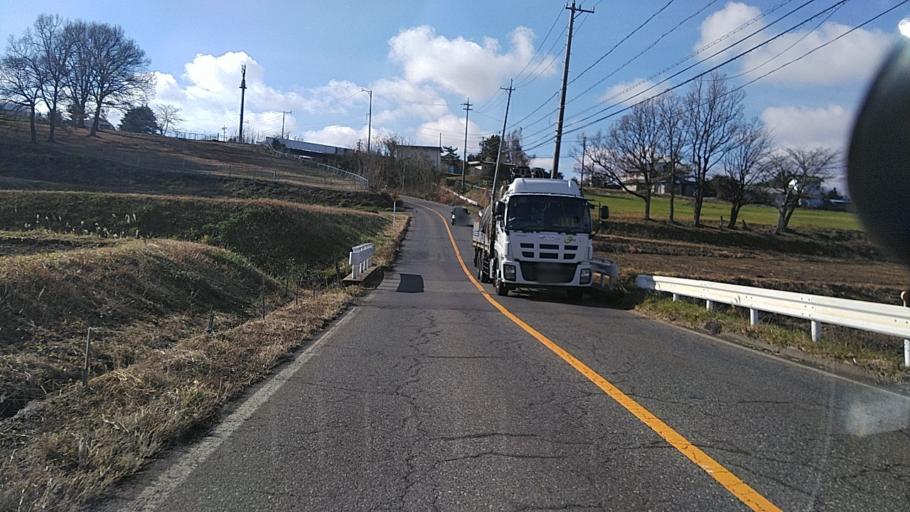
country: JP
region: Nagano
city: Shiojiri
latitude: 36.1248
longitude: 137.9808
